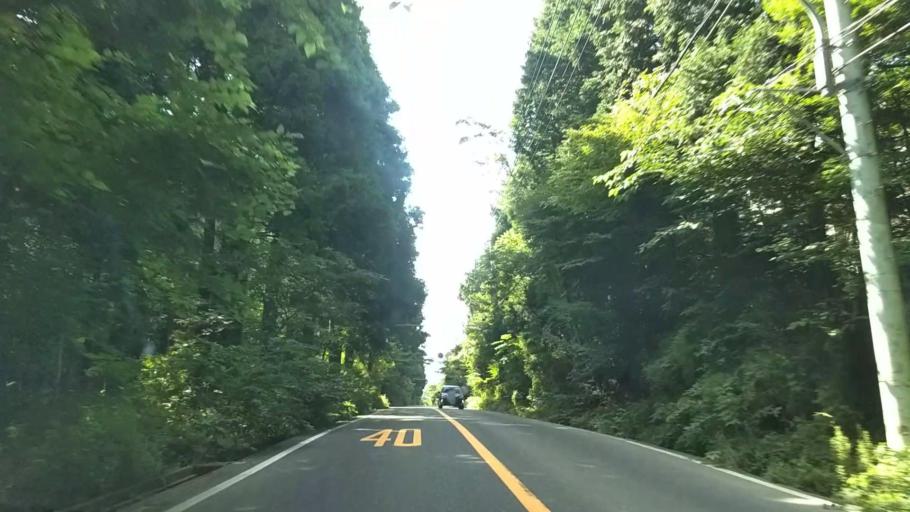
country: JP
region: Kanagawa
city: Hakone
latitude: 35.2062
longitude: 139.0259
